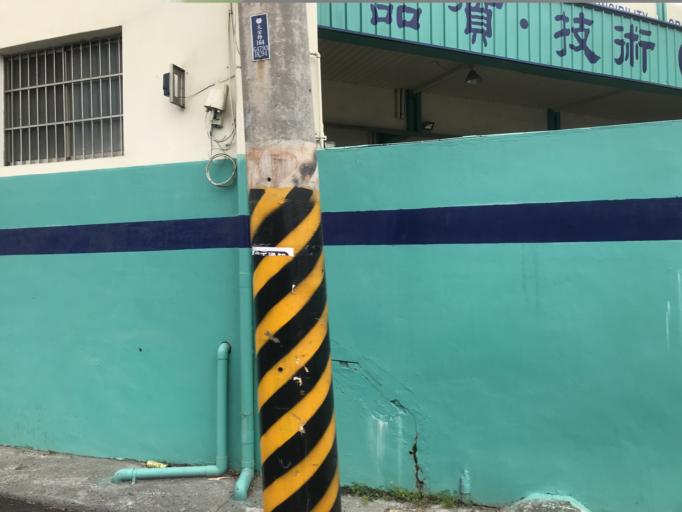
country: TW
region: Taiwan
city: Fengyuan
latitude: 24.3743
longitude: 120.5981
